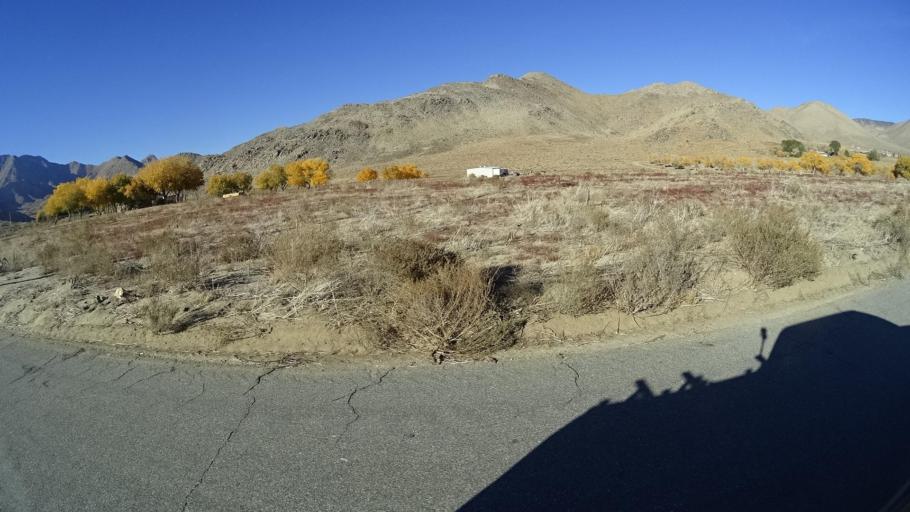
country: US
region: California
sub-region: Kern County
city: Weldon
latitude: 35.5575
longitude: -118.2339
